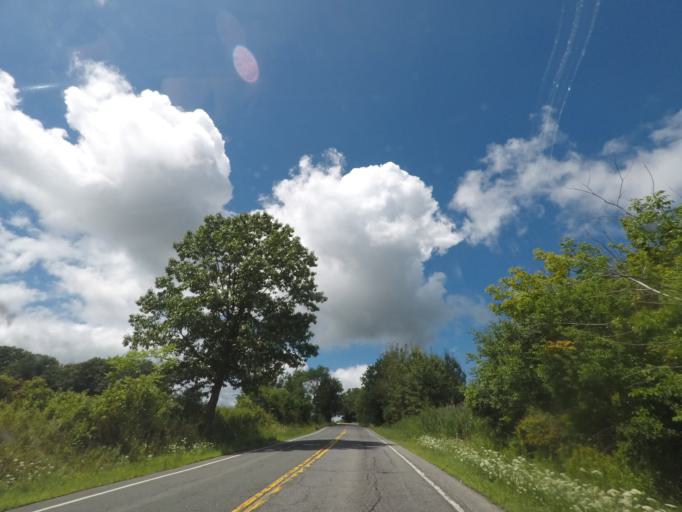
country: US
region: New York
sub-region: Rensselaer County
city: Wynantskill
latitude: 42.6699
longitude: -73.6632
